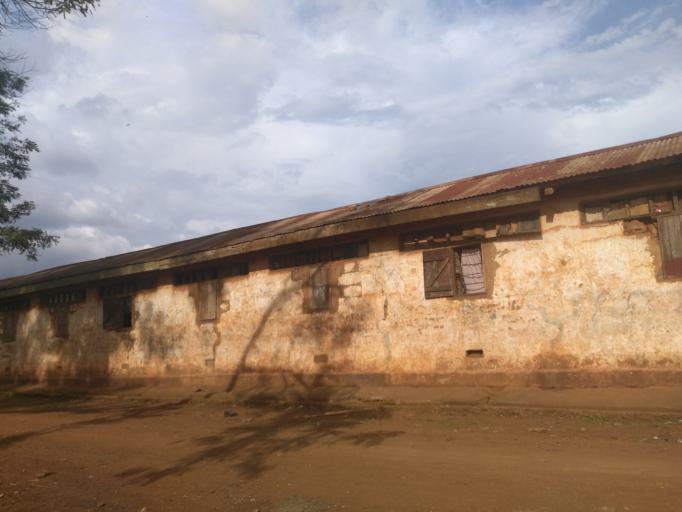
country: UG
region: Eastern Region
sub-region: Jinja District
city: Jinja
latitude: 0.4169
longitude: 33.2159
